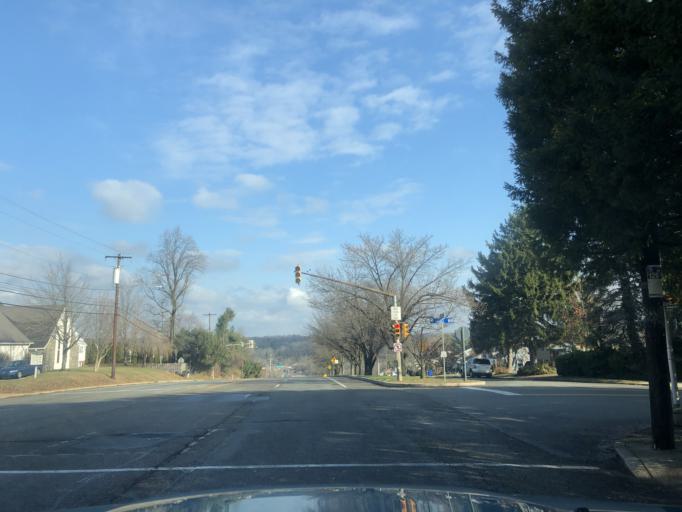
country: US
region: Pennsylvania
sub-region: Delaware County
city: Broomall
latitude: 39.9715
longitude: -75.3440
